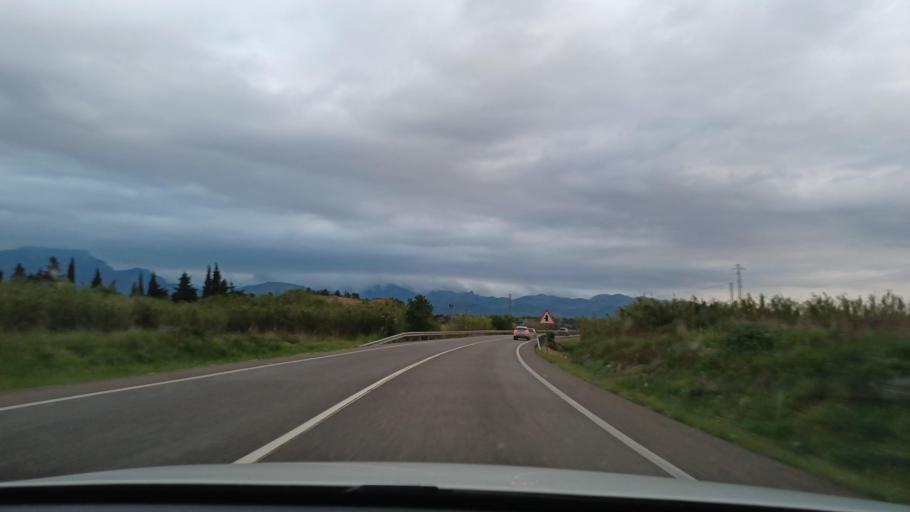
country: ES
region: Catalonia
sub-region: Provincia de Tarragona
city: Tortosa
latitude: 40.7876
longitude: 0.4974
